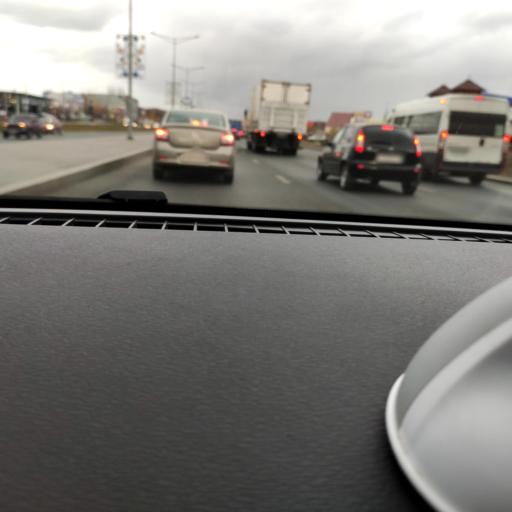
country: RU
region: Samara
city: Petra-Dubrava
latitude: 53.2691
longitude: 50.2544
